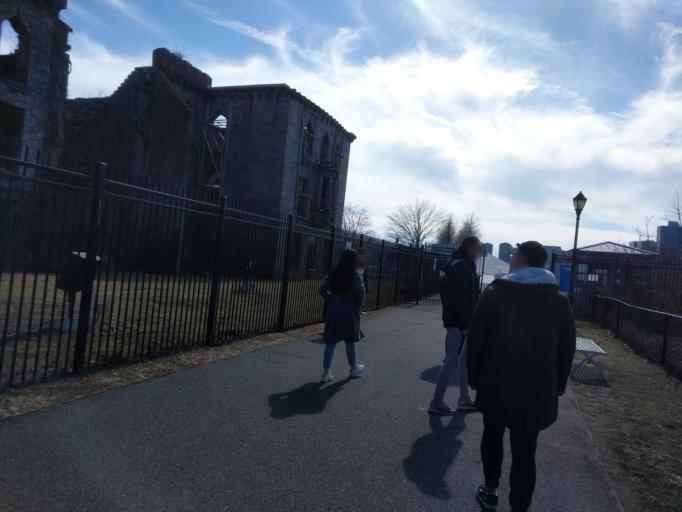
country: US
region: New York
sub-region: Queens County
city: Long Island City
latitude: 40.7520
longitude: -73.9596
